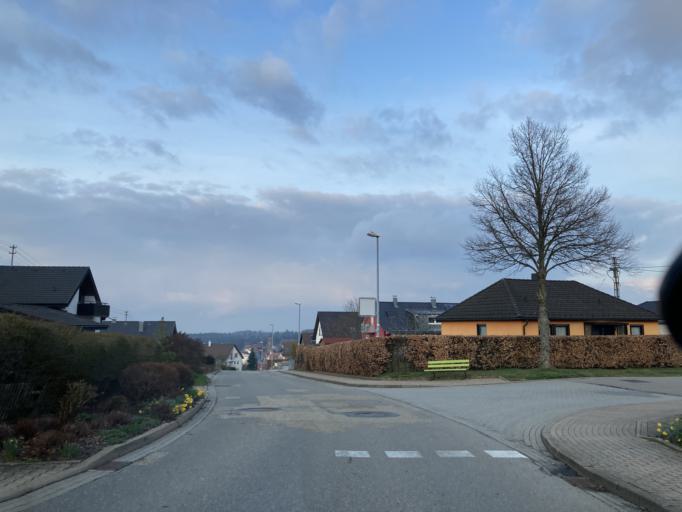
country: DE
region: Baden-Wuerttemberg
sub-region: Karlsruhe Region
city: Schomberg
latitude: 48.7850
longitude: 8.6373
